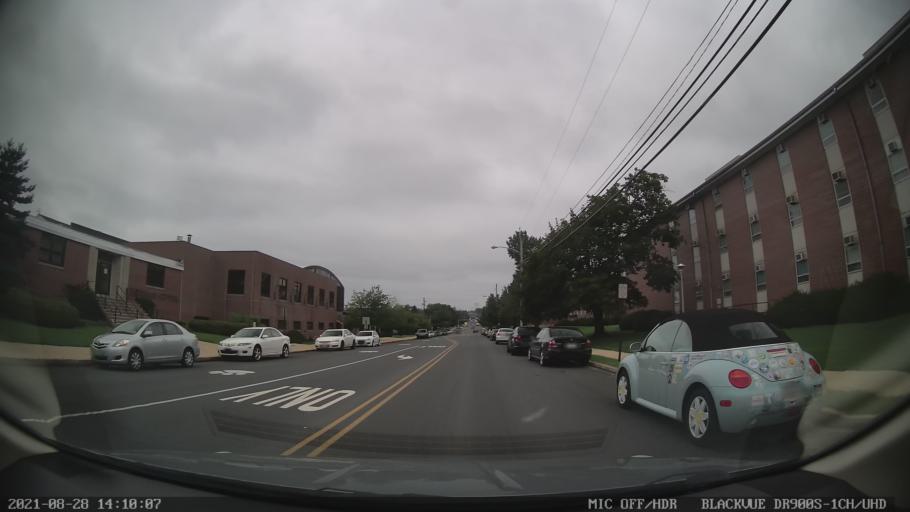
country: US
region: Pennsylvania
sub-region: Berks County
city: Hyde Park
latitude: 40.3623
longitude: -75.9115
